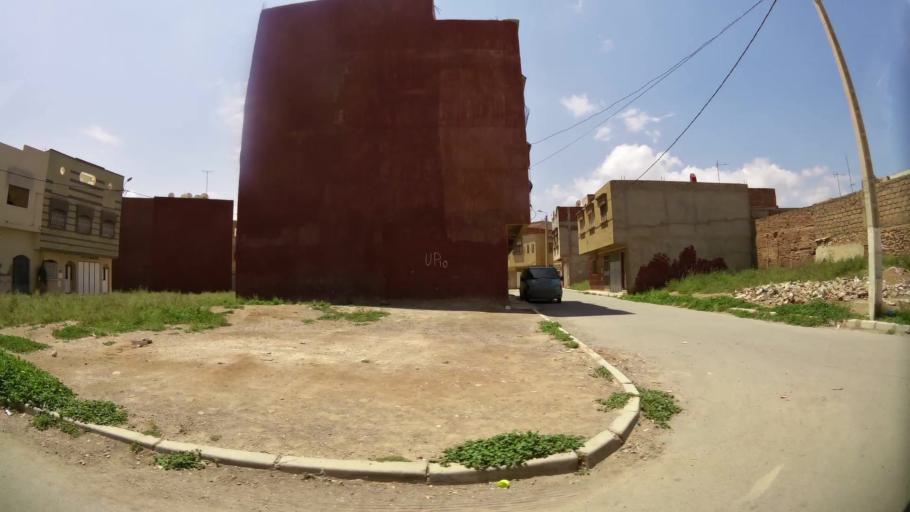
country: MA
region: Oriental
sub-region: Oujda-Angad
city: Oujda
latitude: 34.6841
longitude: -1.9007
